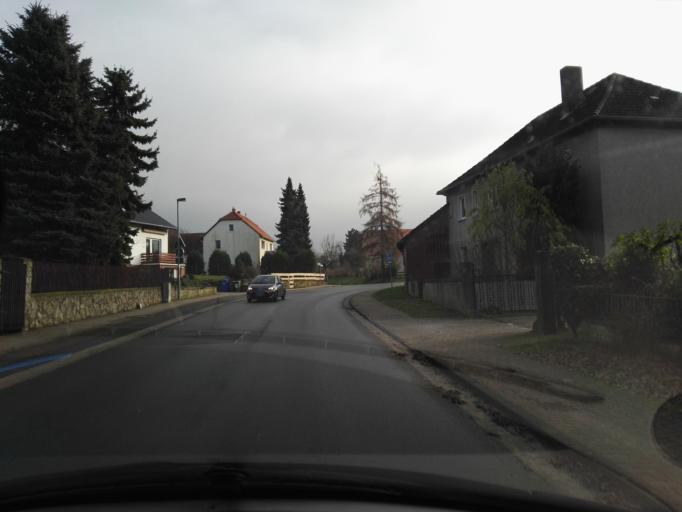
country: DE
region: Lower Saxony
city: Betheln
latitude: 52.0900
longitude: 9.8252
